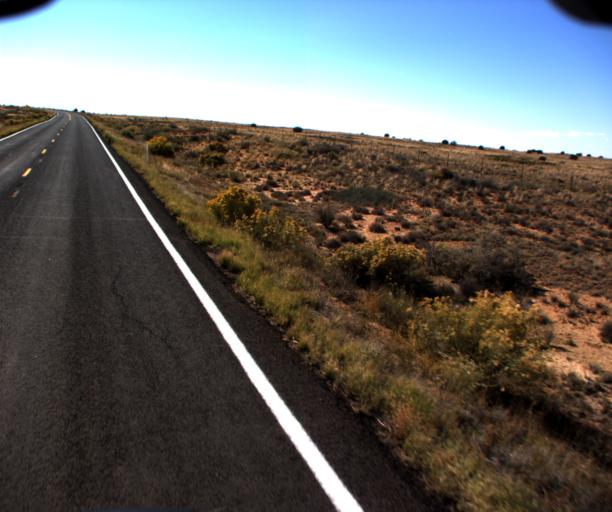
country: US
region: Arizona
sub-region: Coconino County
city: Tuba City
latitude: 35.9645
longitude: -110.8484
